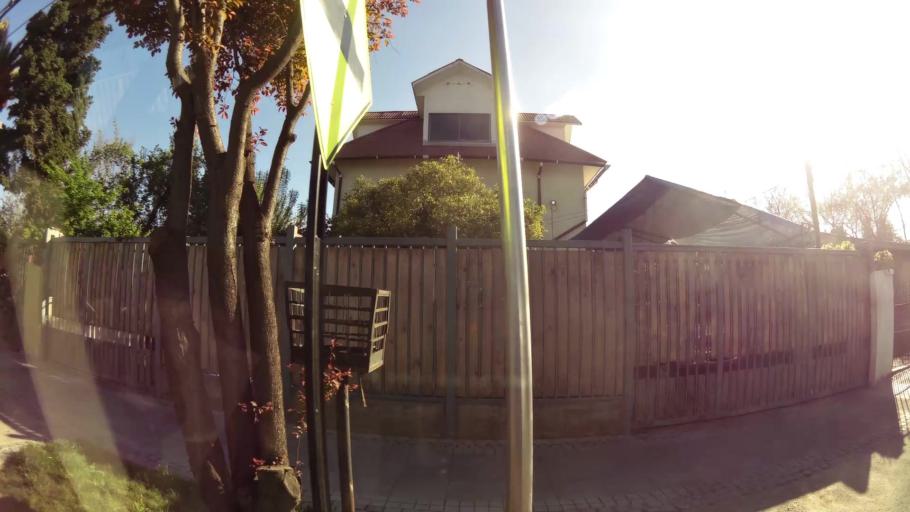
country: CL
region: Santiago Metropolitan
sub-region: Provincia de Santiago
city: Villa Presidente Frei, Nunoa, Santiago, Chile
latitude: -33.4582
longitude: -70.5696
